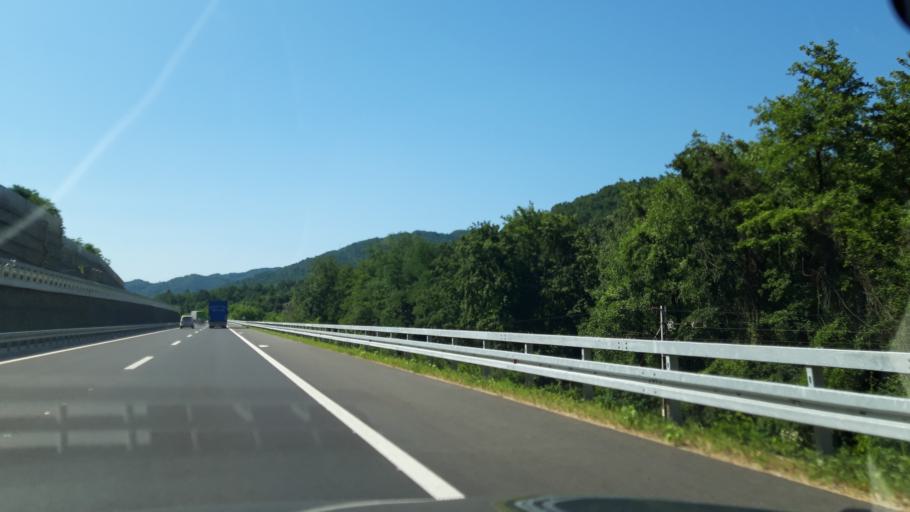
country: RS
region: Central Serbia
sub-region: Jablanicki Okrug
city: Vlasotince
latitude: 42.8514
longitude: 22.1278
